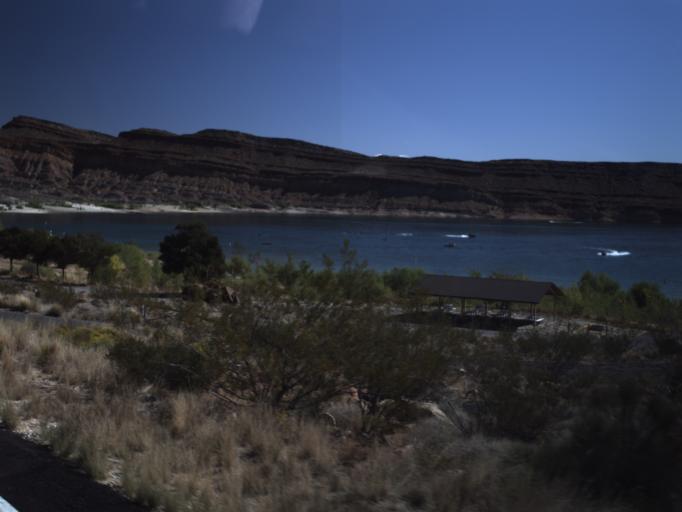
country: US
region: Utah
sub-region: Washington County
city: Hurricane
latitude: 37.1882
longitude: -113.3949
